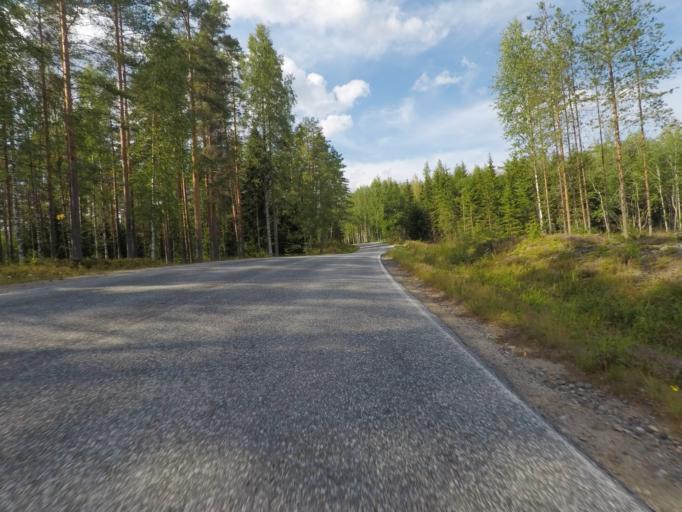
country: FI
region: Southern Savonia
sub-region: Mikkeli
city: Puumala
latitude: 61.6981
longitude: 28.2126
